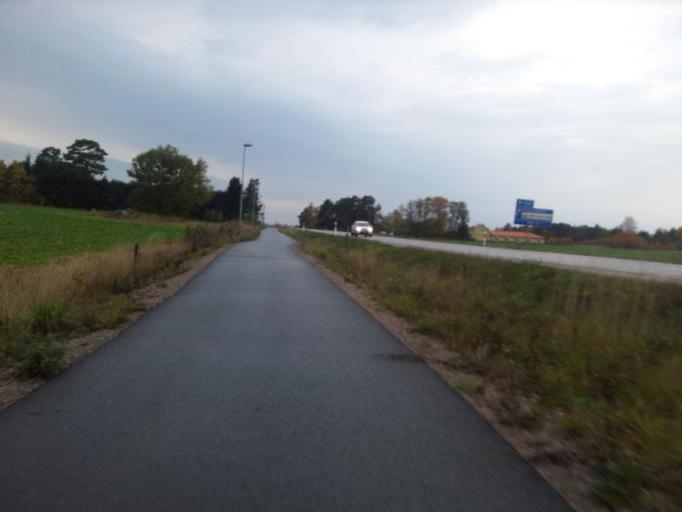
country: SE
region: Uppsala
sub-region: Uppsala Kommun
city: Gamla Uppsala
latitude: 59.8950
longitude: 17.7050
